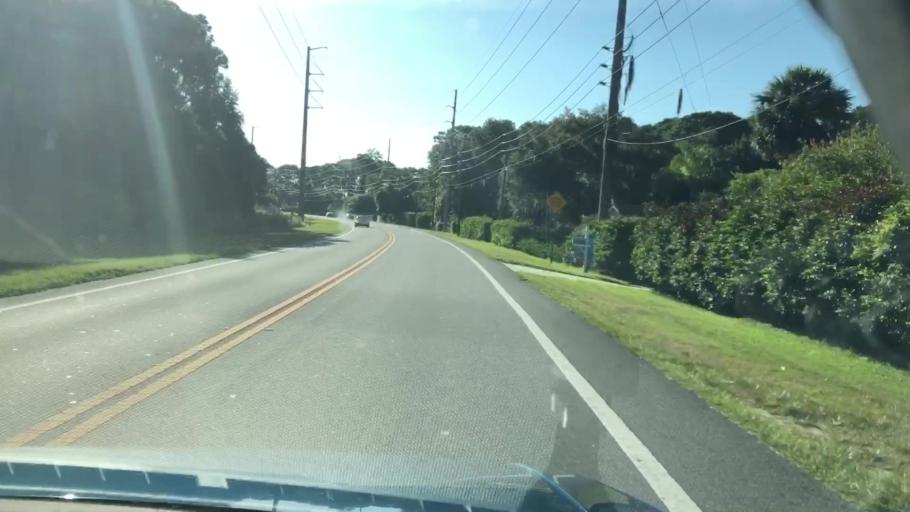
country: US
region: Florida
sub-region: Lake County
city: Eustis
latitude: 28.8747
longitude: -81.7058
